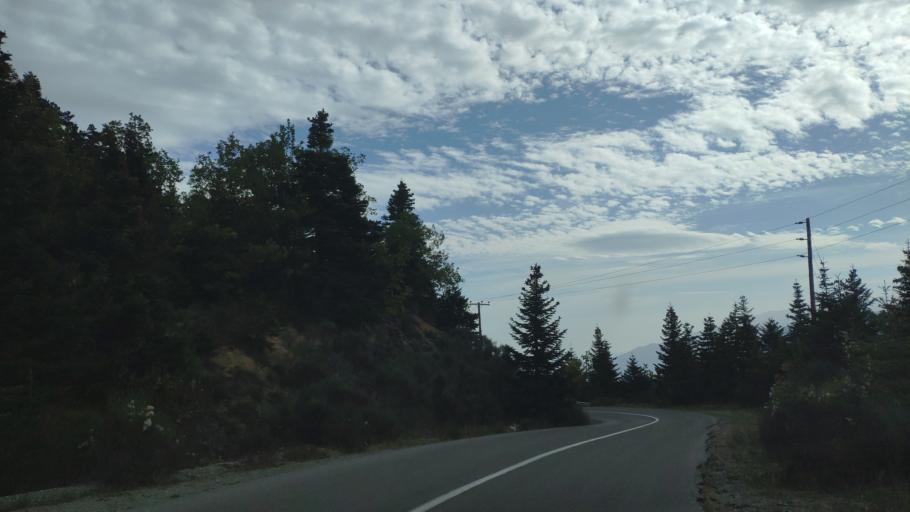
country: GR
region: Central Greece
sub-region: Nomos Fokidos
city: Amfissa
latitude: 38.7061
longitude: 22.3254
